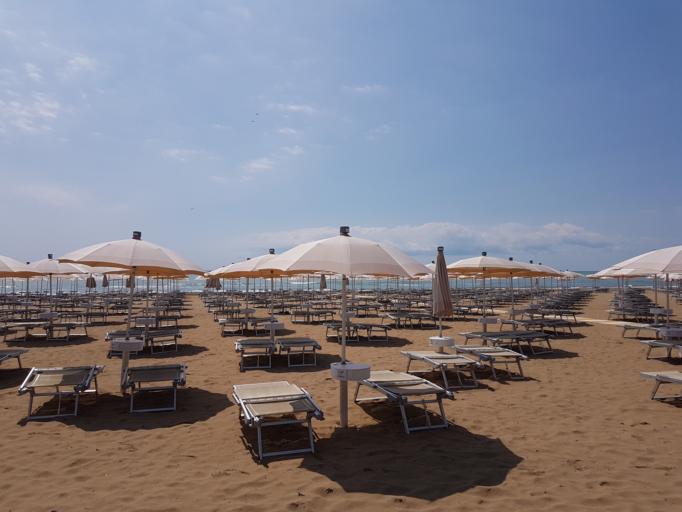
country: IT
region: Veneto
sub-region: Provincia di Venezia
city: Lido di Iesolo
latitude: 45.5073
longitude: 12.6540
